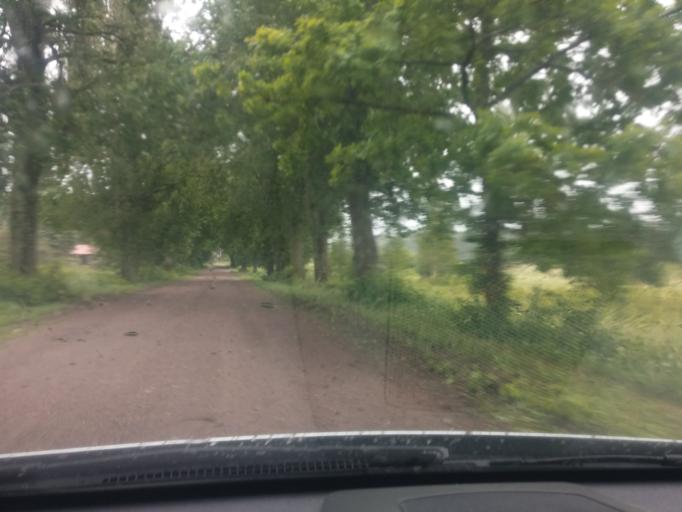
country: LV
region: Ogre
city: Ogre
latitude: 56.8628
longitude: 24.5787
